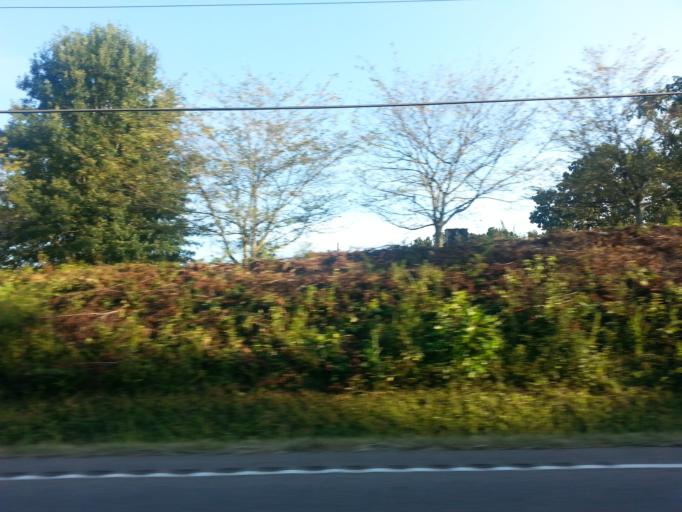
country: US
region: Tennessee
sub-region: McMinn County
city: Englewood
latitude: 35.4262
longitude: -84.5052
